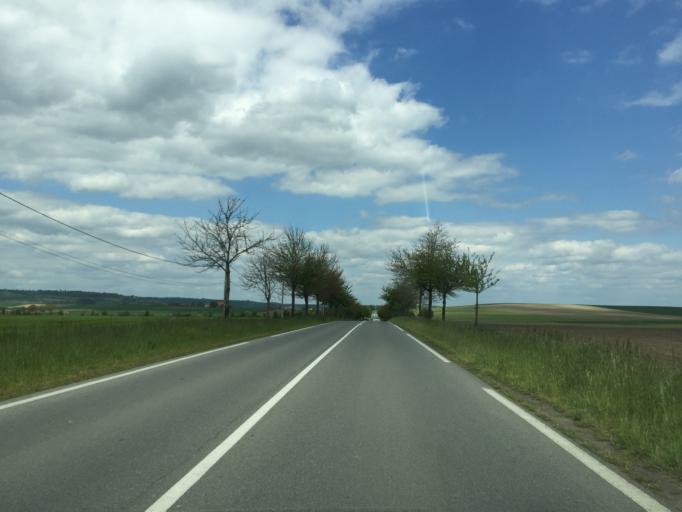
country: FR
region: Auvergne
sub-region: Departement du Puy-de-Dome
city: Aigueperse
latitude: 45.9825
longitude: 3.1833
